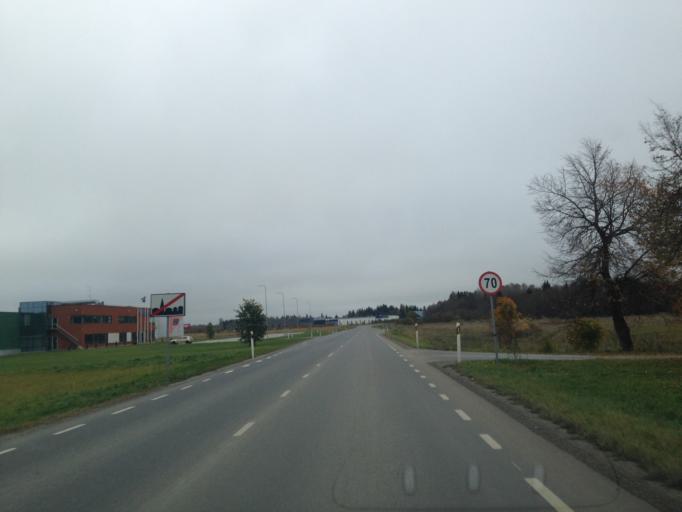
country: EE
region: Harju
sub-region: Harku vald
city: Tabasalu
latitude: 59.4205
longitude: 24.5396
